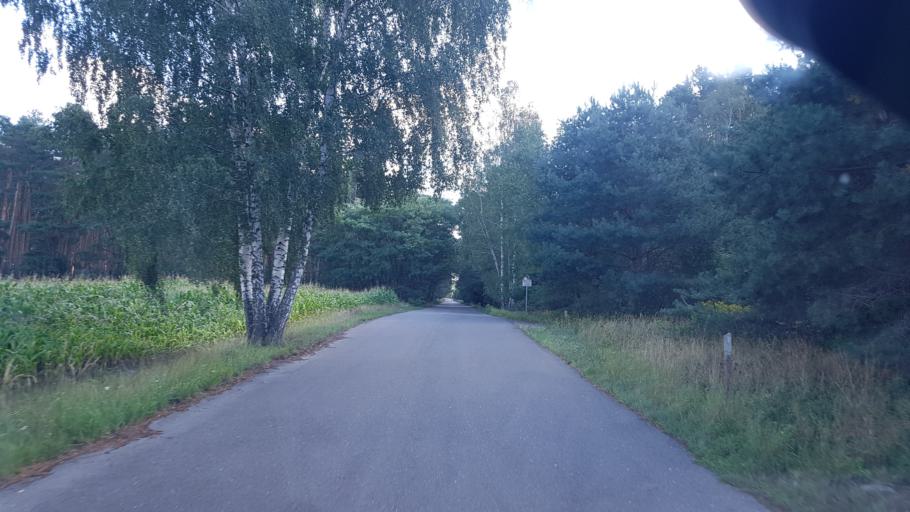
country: DE
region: Brandenburg
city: Drebkau
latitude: 51.6525
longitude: 14.2562
